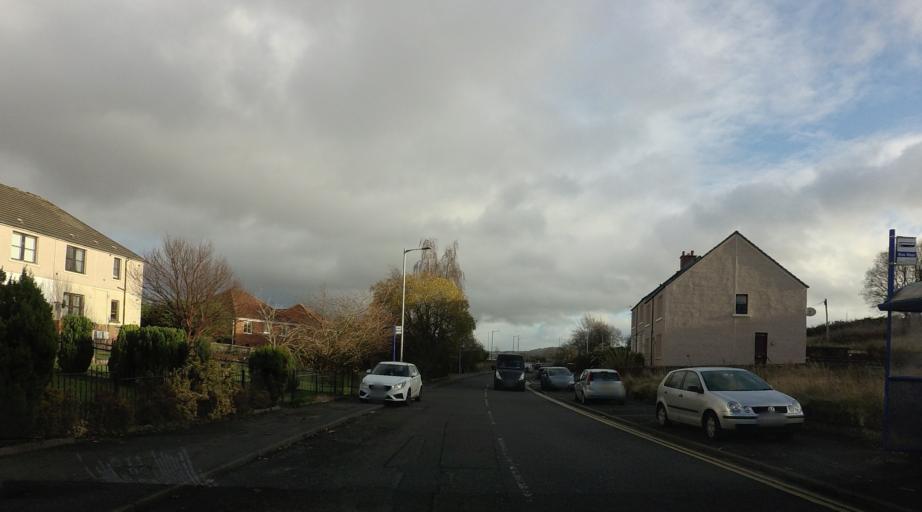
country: GB
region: Scotland
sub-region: Falkirk
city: Polmont
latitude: 55.9746
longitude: -3.7051
